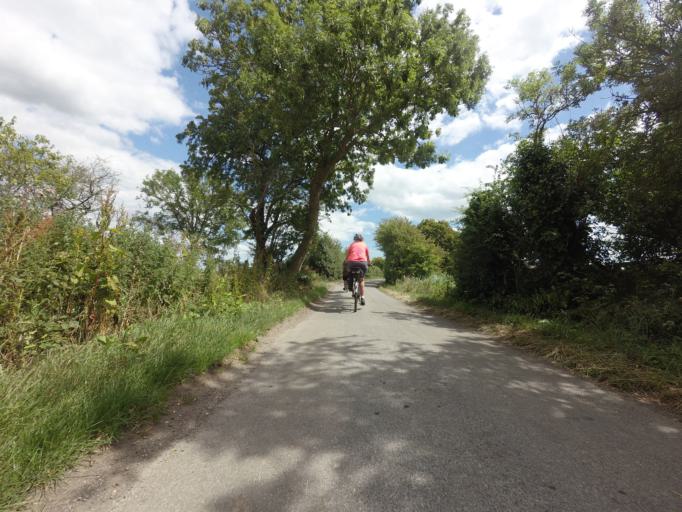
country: GB
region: England
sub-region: East Sussex
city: Pevensey
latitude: 50.8389
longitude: 0.3104
